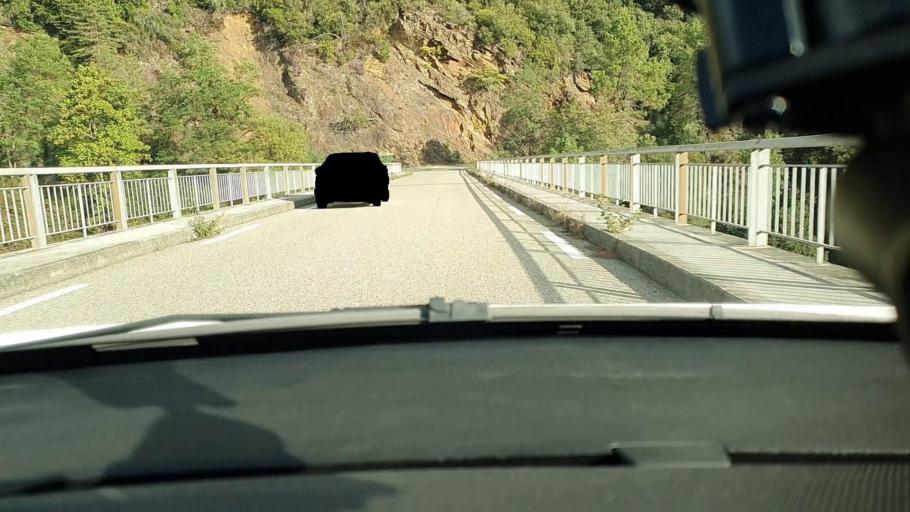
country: FR
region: Languedoc-Roussillon
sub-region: Departement du Gard
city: Besseges
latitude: 44.3190
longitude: 4.0378
